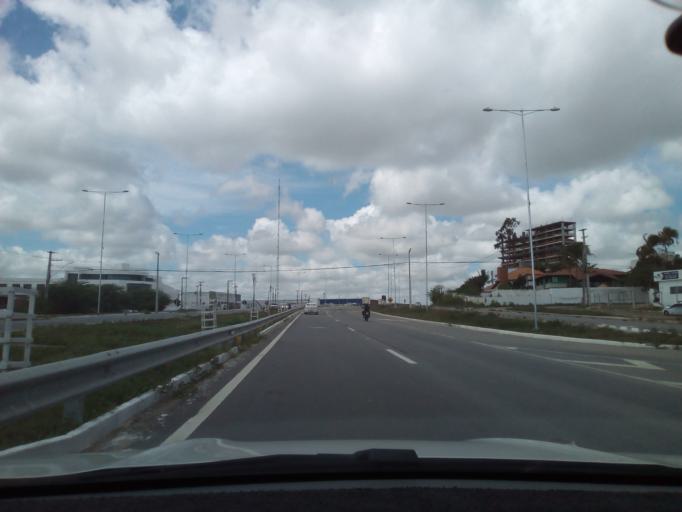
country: BR
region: Paraiba
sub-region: Campina Grande
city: Campina Grande
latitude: -7.2480
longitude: -35.8716
